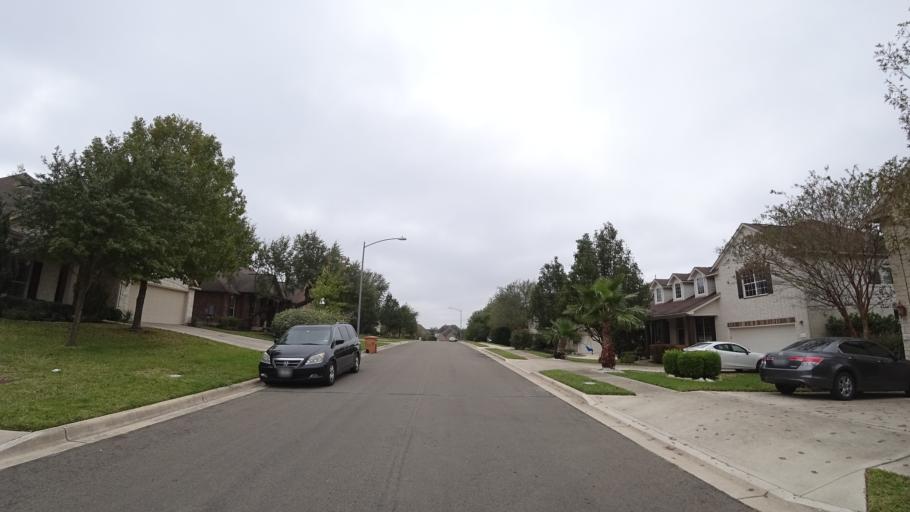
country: US
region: Texas
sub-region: Travis County
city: Barton Creek
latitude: 30.2383
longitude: -97.9008
